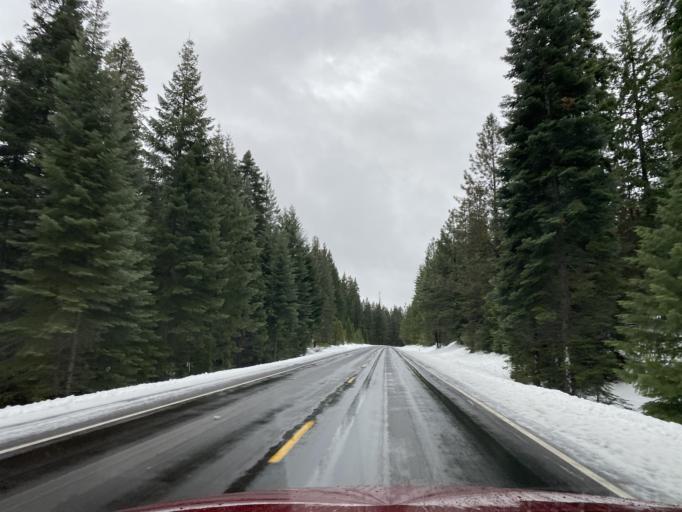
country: US
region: Oregon
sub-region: Klamath County
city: Klamath Falls
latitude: 42.5061
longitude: -122.0830
